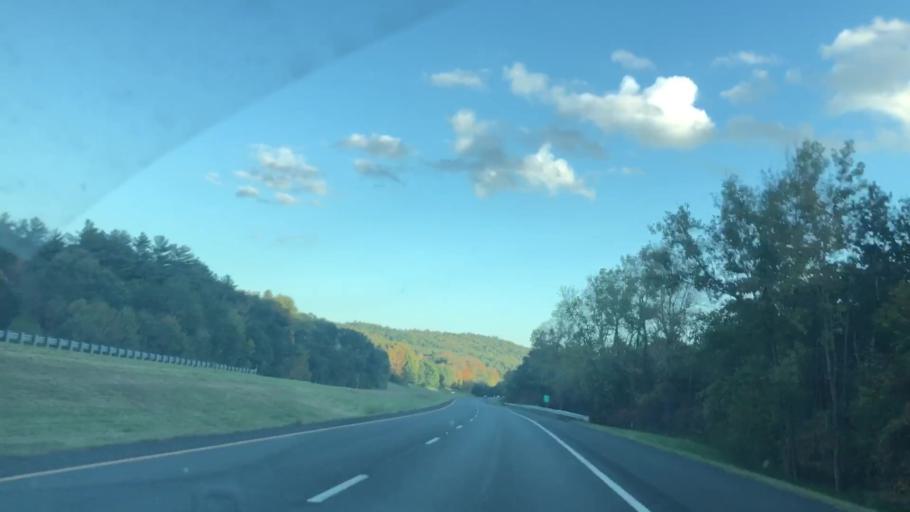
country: US
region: Massachusetts
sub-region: Franklin County
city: Bernardston
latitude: 42.7004
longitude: -72.5550
